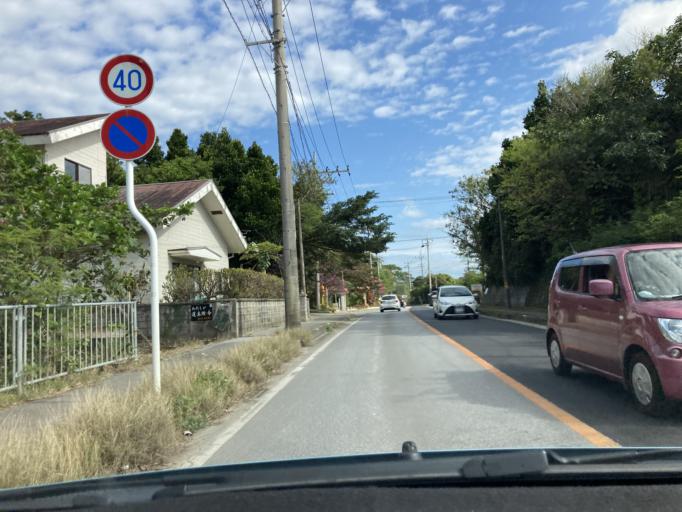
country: JP
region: Okinawa
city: Nago
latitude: 26.7001
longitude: 127.9293
